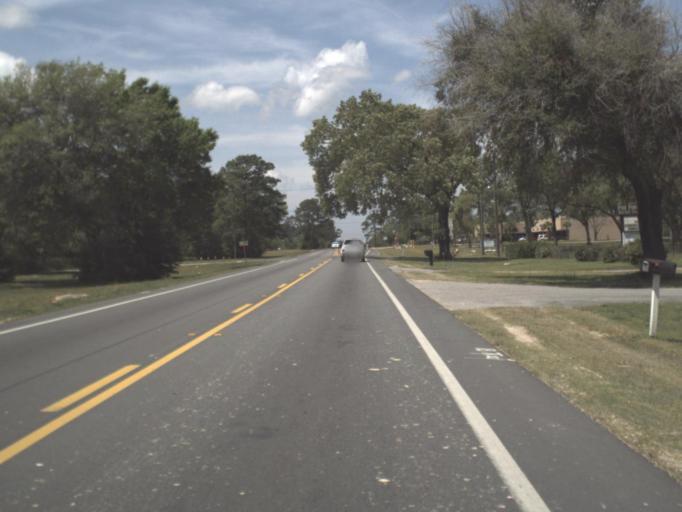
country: US
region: Florida
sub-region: Escambia County
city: Ensley
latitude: 30.5344
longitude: -87.3190
